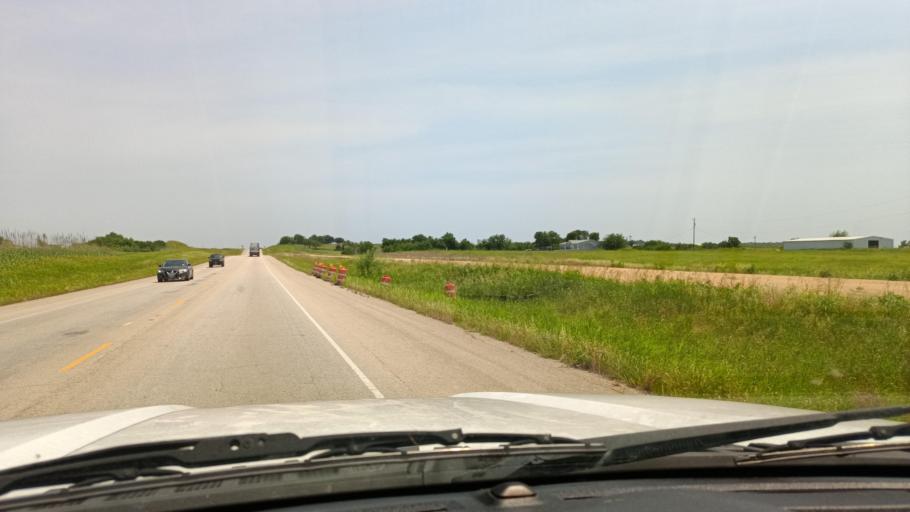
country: US
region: Texas
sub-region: Bell County
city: Rogers
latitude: 30.9747
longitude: -97.2709
